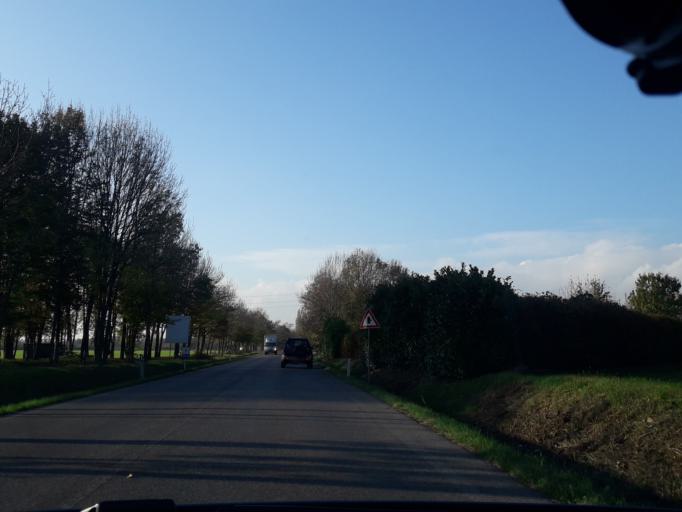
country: IT
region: Friuli Venezia Giulia
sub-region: Provincia di Udine
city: Pradamano
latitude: 46.0441
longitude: 13.2822
